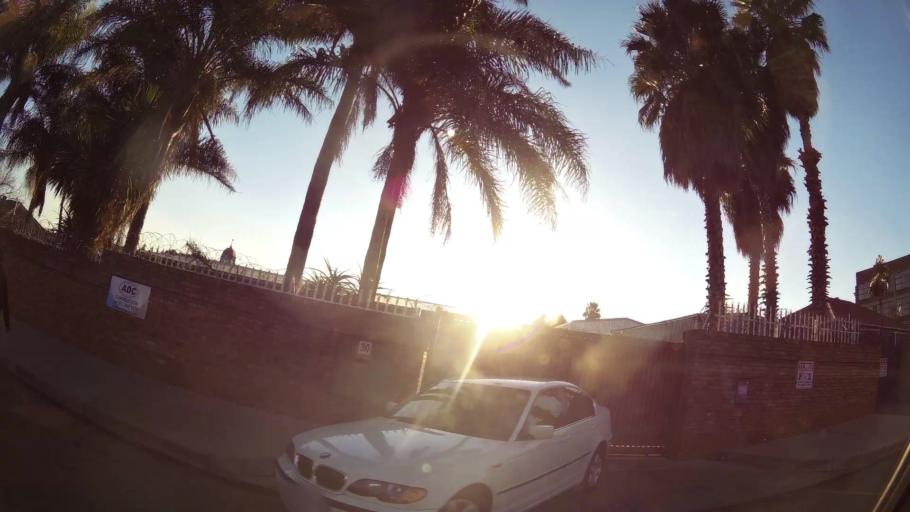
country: ZA
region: Gauteng
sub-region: Ekurhuleni Metropolitan Municipality
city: Germiston
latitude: -26.2565
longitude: 28.1304
